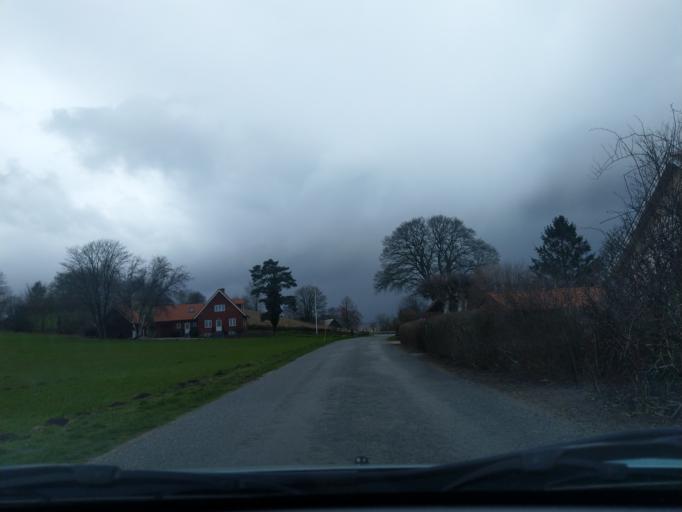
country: DK
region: Zealand
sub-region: Soro Kommune
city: Frederiksberg
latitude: 55.3613
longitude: 11.5697
